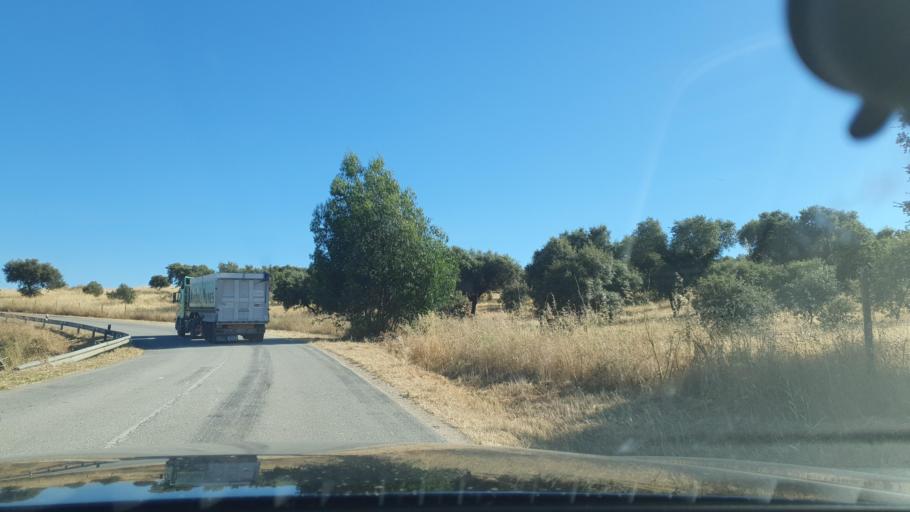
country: PT
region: Evora
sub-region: Alandroal
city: Alandroal
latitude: 38.7293
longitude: -7.4053
